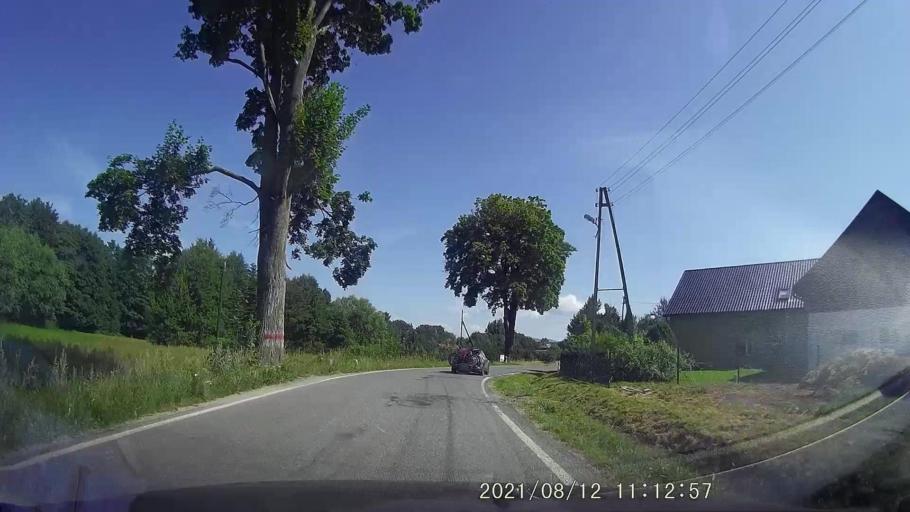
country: PL
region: Lower Silesian Voivodeship
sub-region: Powiat klodzki
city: Bystrzyca Klodzka
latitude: 50.3477
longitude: 16.5878
